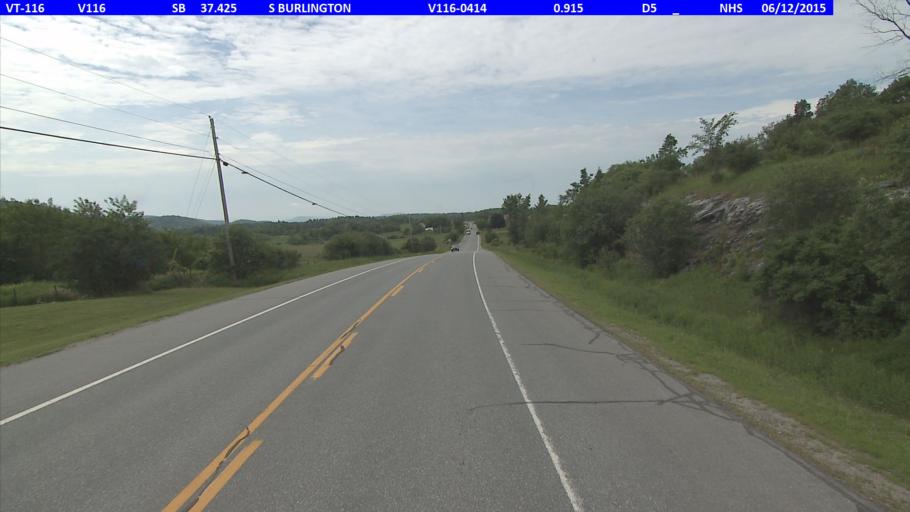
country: US
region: Vermont
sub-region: Chittenden County
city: South Burlington
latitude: 44.4231
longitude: -73.1542
